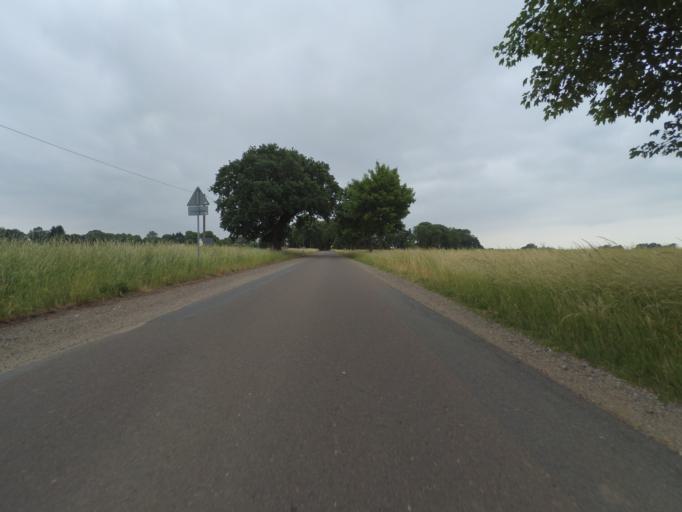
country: DE
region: Mecklenburg-Vorpommern
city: Spornitz
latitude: 53.3586
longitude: 11.7289
